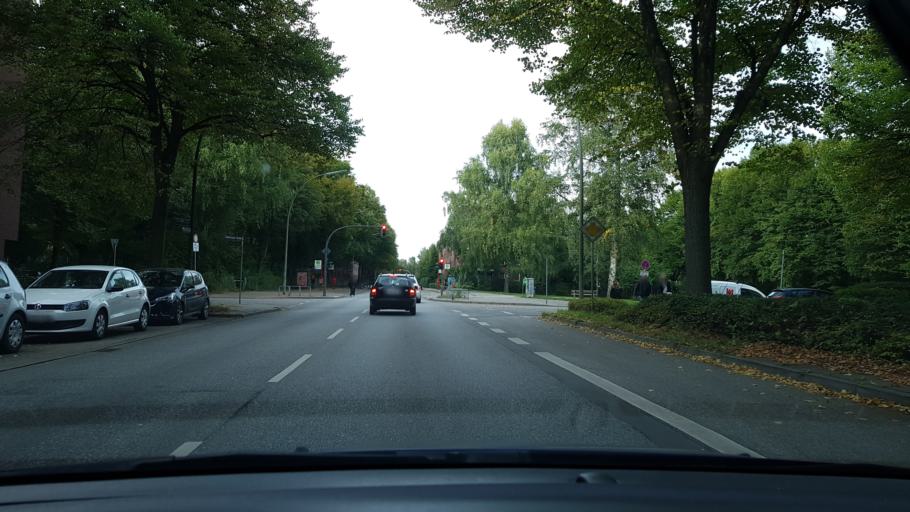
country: DE
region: Hamburg
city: Barmbek-Nord
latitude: 53.5989
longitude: 10.0507
